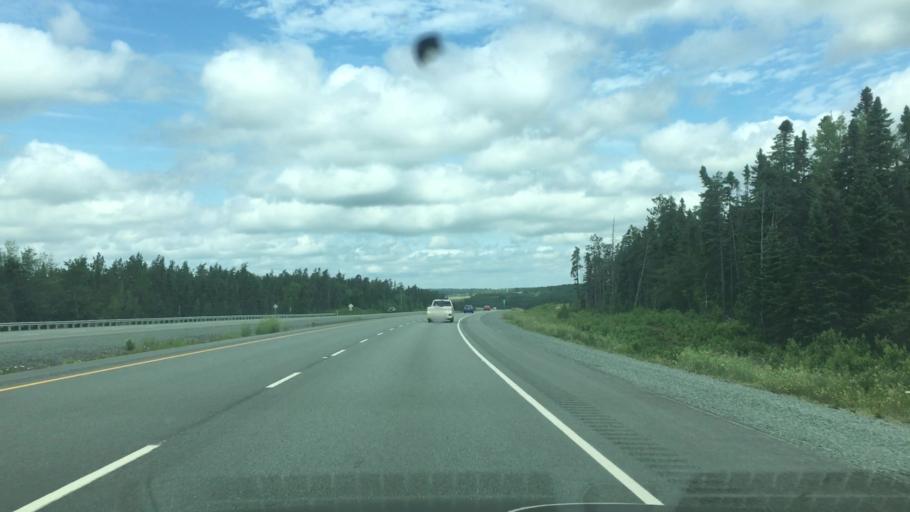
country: CA
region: Nova Scotia
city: Oxford
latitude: 45.6743
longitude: -63.7591
